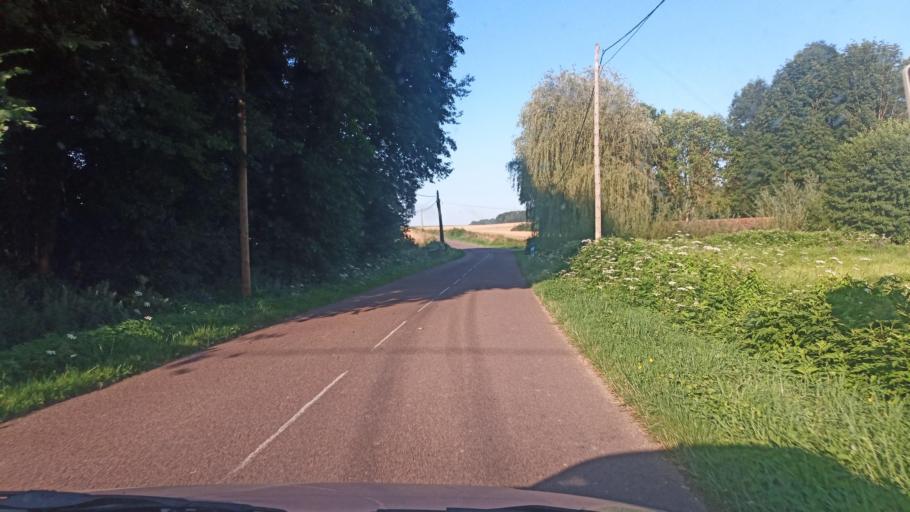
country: FR
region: Bourgogne
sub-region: Departement de l'Yonne
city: Saint-Valerien
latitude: 48.1889
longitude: 3.1090
